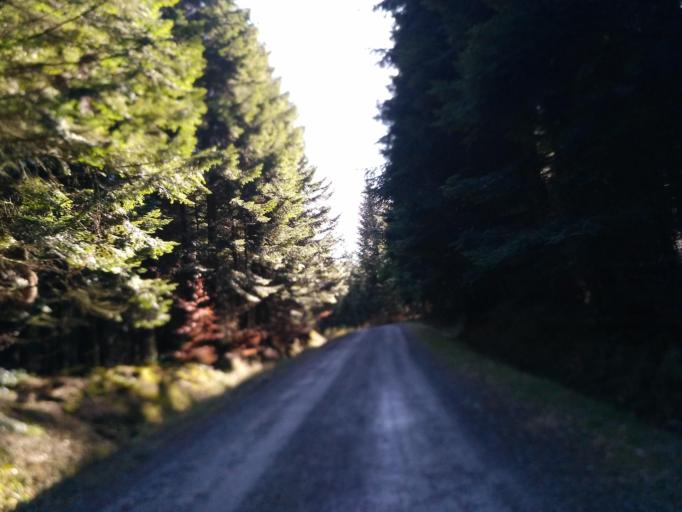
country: PL
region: Subcarpathian Voivodeship
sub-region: Powiat strzyzowski
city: Babica
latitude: 49.9540
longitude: 21.8677
